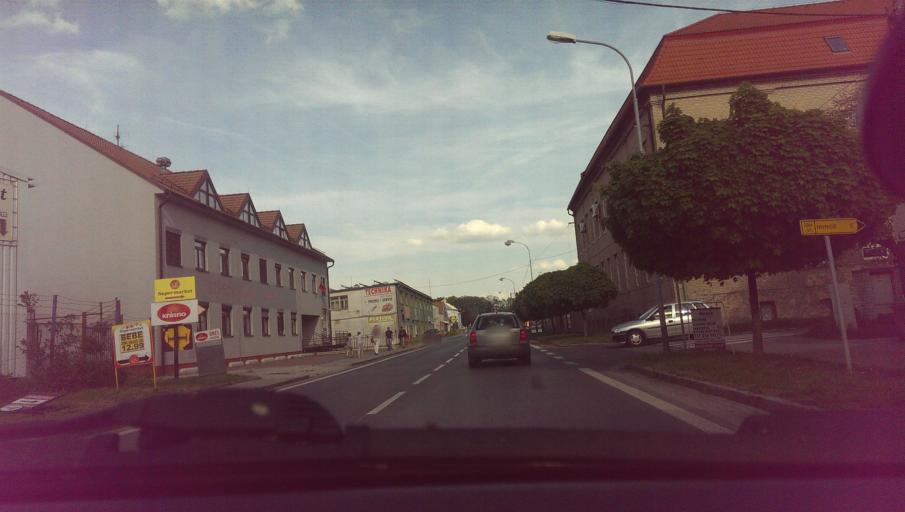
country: CZ
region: Zlin
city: Uhersky Brod
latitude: 49.0206
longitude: 17.6430
